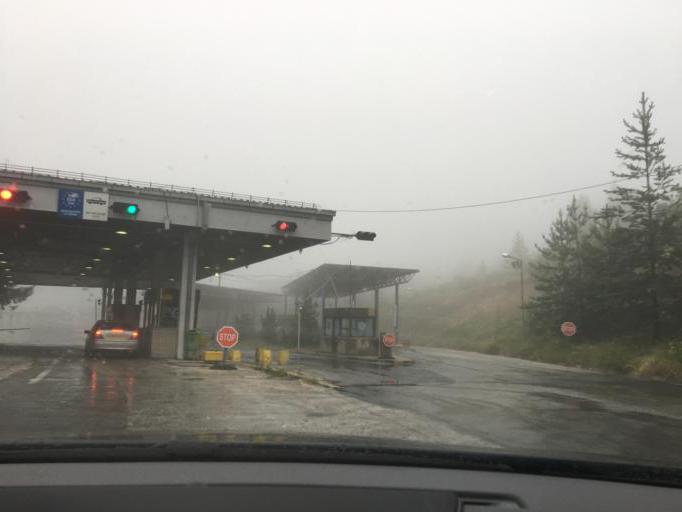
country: MK
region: Kriva Palanka
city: Kriva Palanka
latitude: 42.2202
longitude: 22.4592
